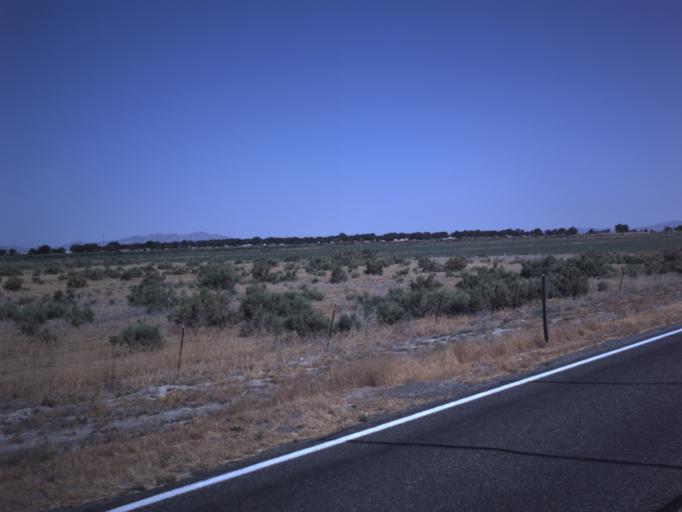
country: US
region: Utah
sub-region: Millard County
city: Delta
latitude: 39.3079
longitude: -112.6525
